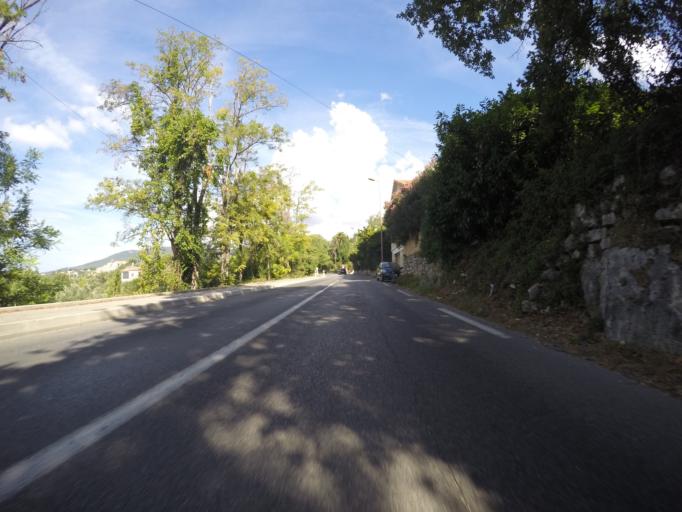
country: FR
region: Provence-Alpes-Cote d'Azur
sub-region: Departement des Alpes-Maritimes
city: Opio
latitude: 43.6744
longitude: 6.9885
